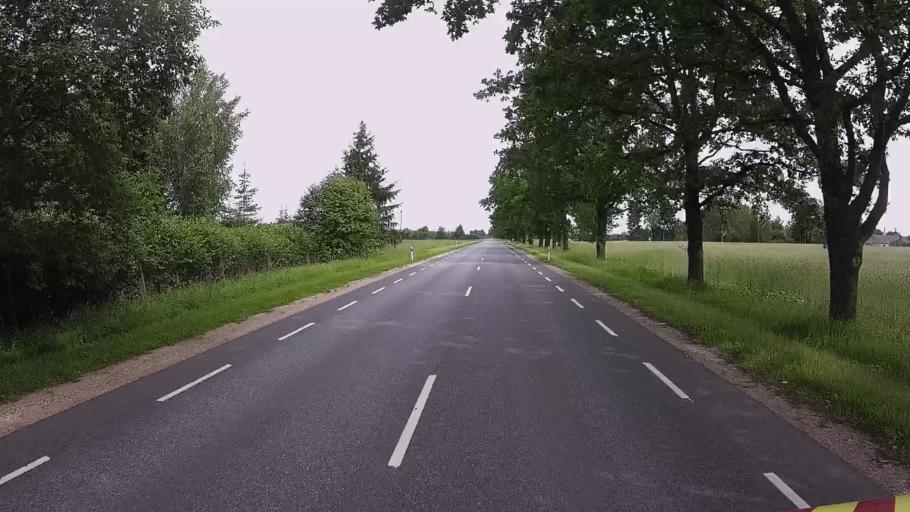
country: EE
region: Viljandimaa
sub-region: Karksi vald
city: Karksi-Nuia
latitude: 58.1225
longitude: 25.5827
